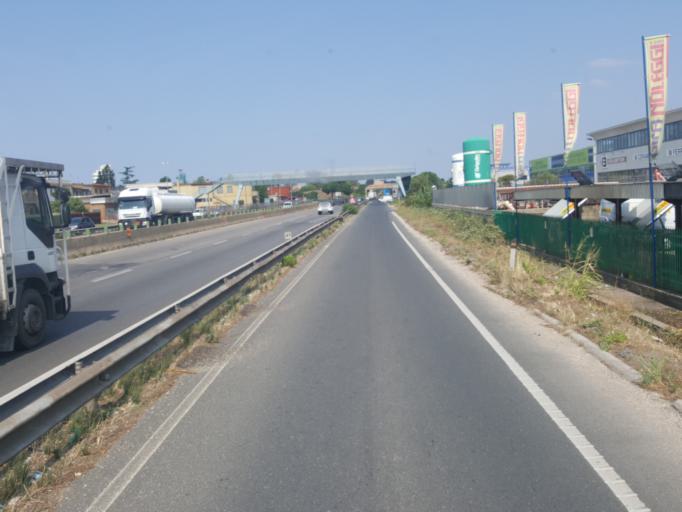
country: IT
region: Latium
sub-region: Provincia di Latina
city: Aprilia
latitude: 41.5757
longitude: 12.6575
